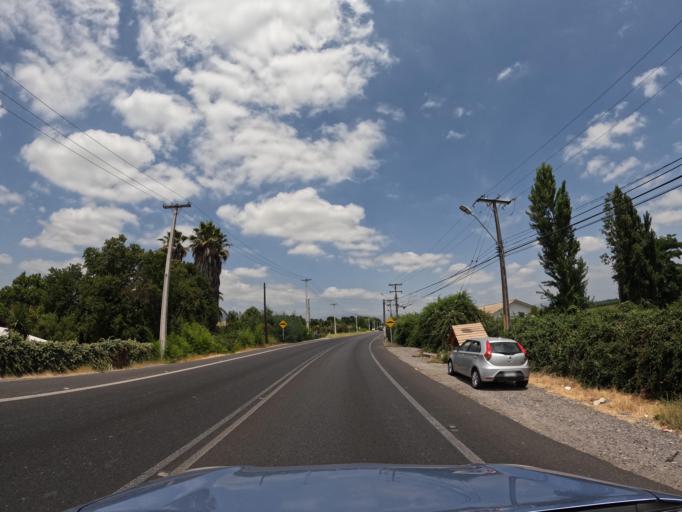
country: CL
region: Maule
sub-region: Provincia de Curico
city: Curico
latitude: -35.0265
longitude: -71.1970
